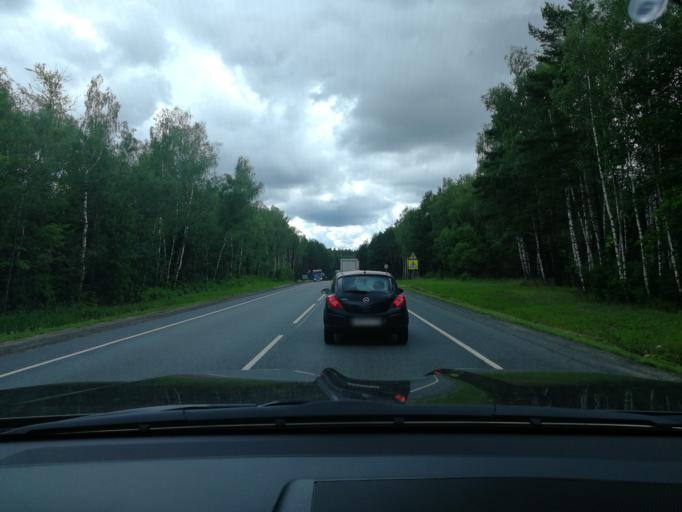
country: RU
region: Moskovskaya
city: Popovo
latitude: 55.0681
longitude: 37.7993
